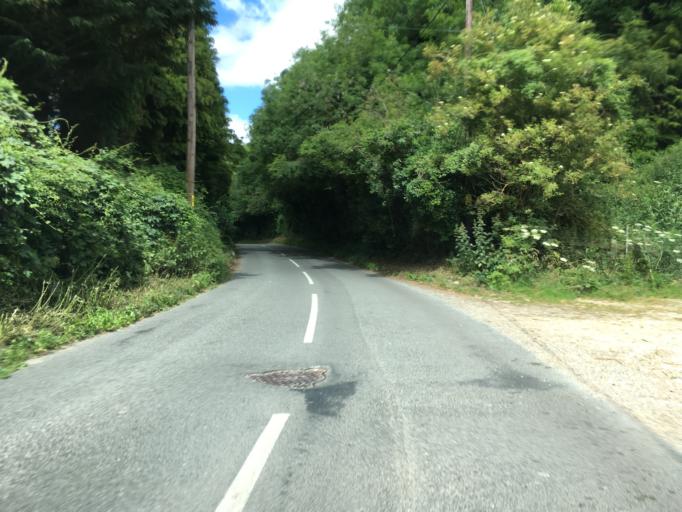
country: GB
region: England
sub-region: Hampshire
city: Highclere
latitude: 51.2415
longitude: -1.3852
